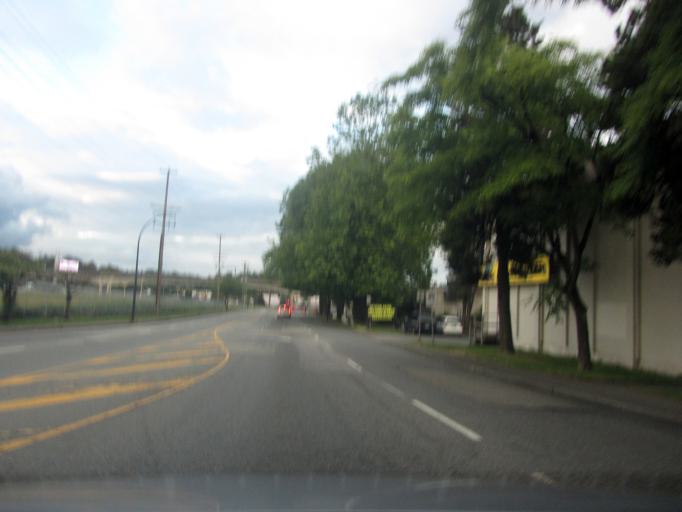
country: CA
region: British Columbia
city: New Westminster
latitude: 49.2315
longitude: -122.8859
